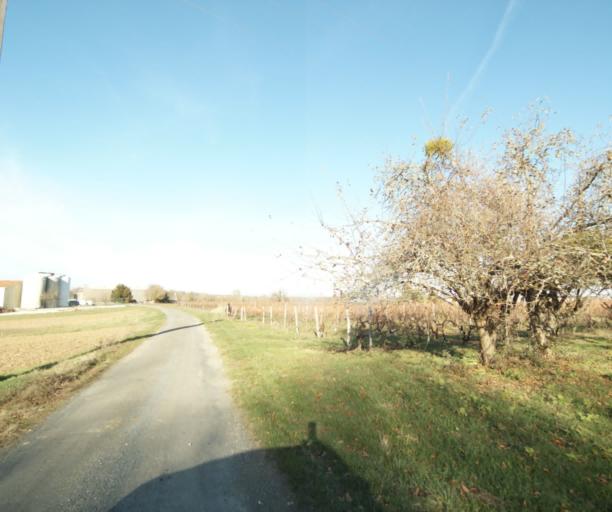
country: FR
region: Poitou-Charentes
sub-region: Departement de la Charente-Maritime
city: Burie
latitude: 45.7823
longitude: -0.4346
